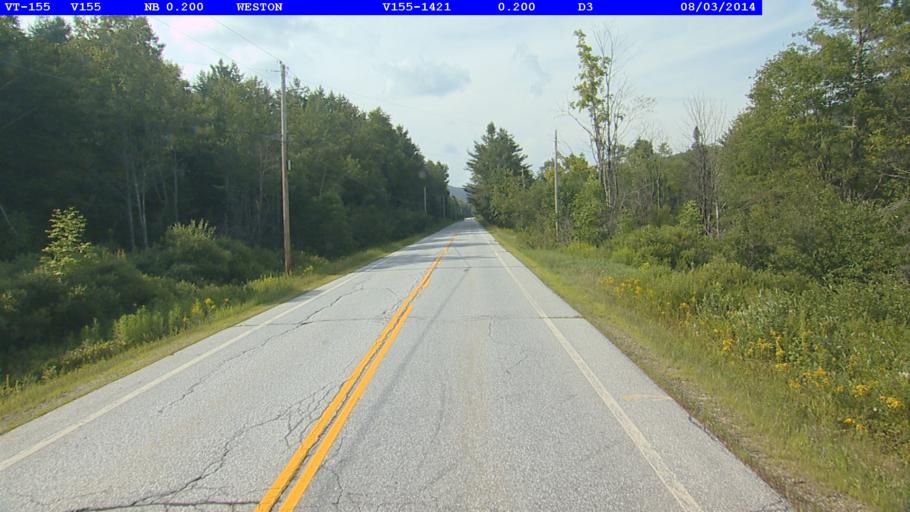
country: US
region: Vermont
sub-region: Windsor County
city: Chester
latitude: 43.3396
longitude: -72.7872
